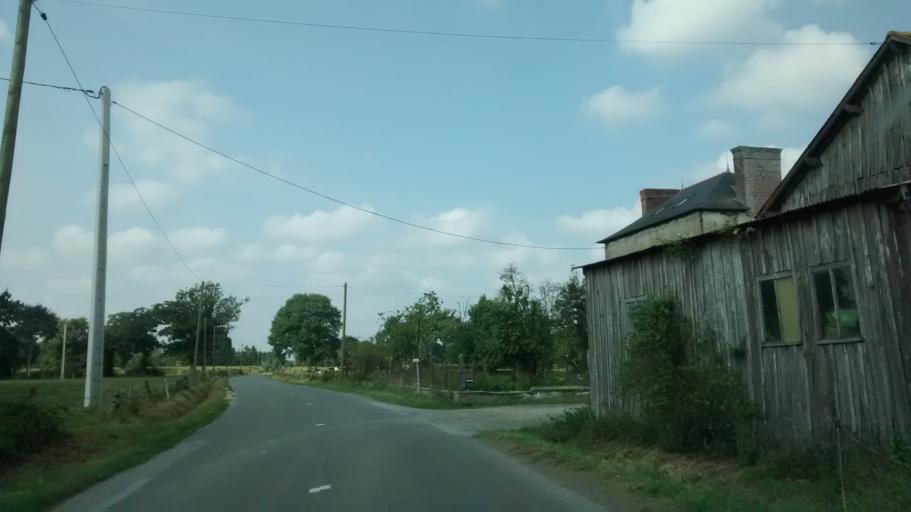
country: FR
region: Brittany
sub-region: Departement d'Ille-et-Vilaine
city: Livre-sur-Changeon
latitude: 48.2326
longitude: -1.2864
